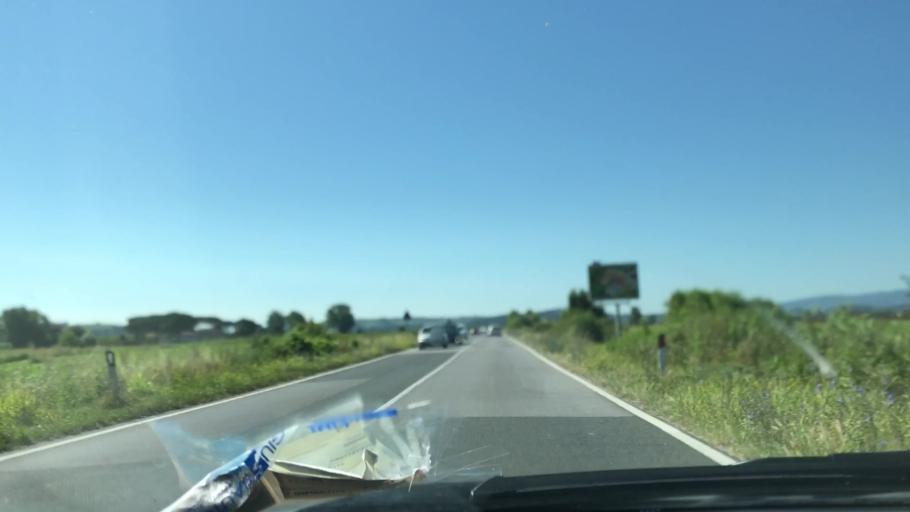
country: IT
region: Tuscany
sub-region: Province of Pisa
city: Forcoli
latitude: 43.5942
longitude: 10.6988
